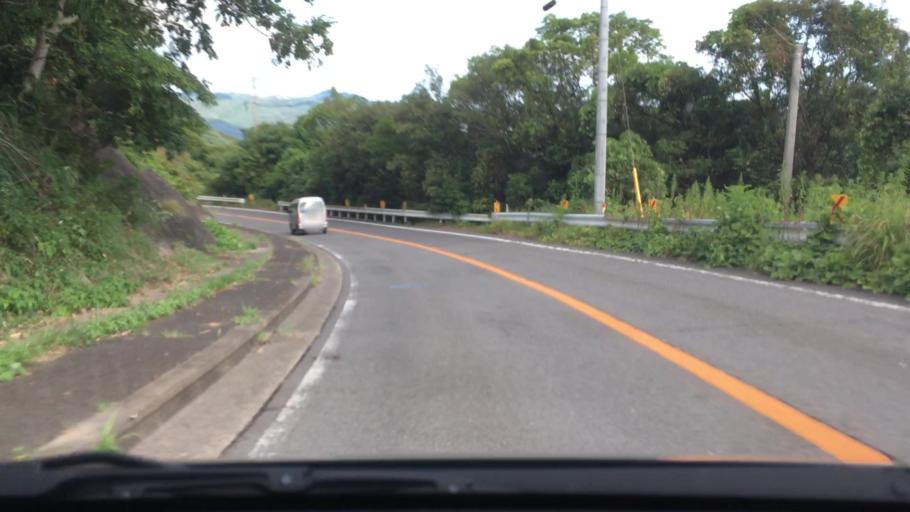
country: JP
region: Nagasaki
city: Togitsu
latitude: 32.8214
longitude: 129.7277
